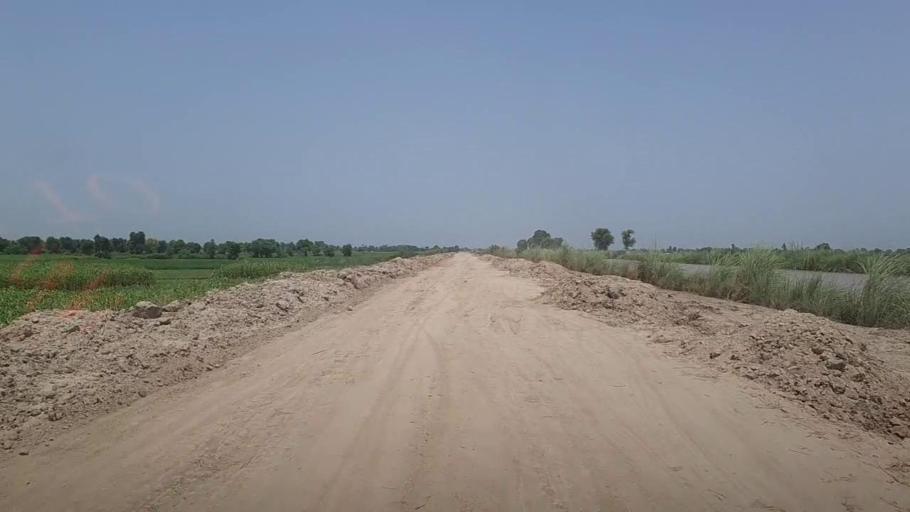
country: PK
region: Sindh
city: Pad Idan
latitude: 26.7986
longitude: 68.2738
